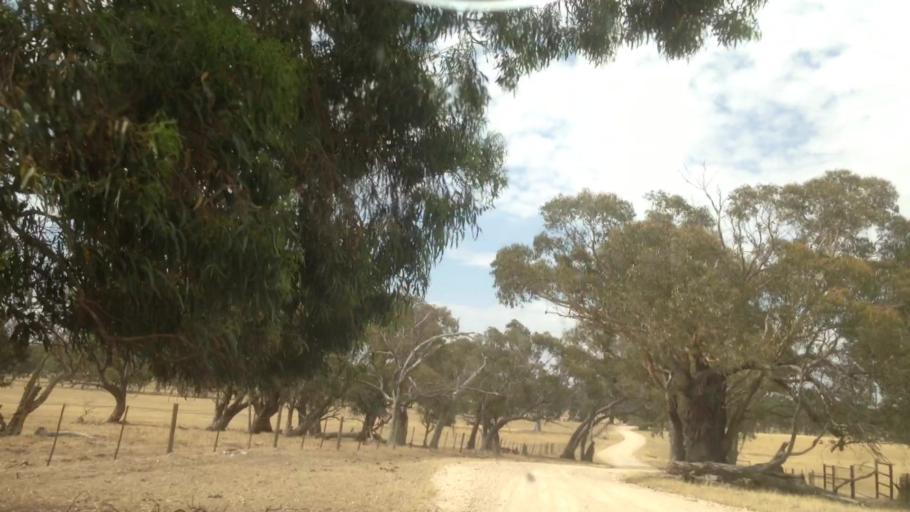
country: AU
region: South Australia
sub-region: Barossa
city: Williamstown
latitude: -34.6951
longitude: 138.9915
